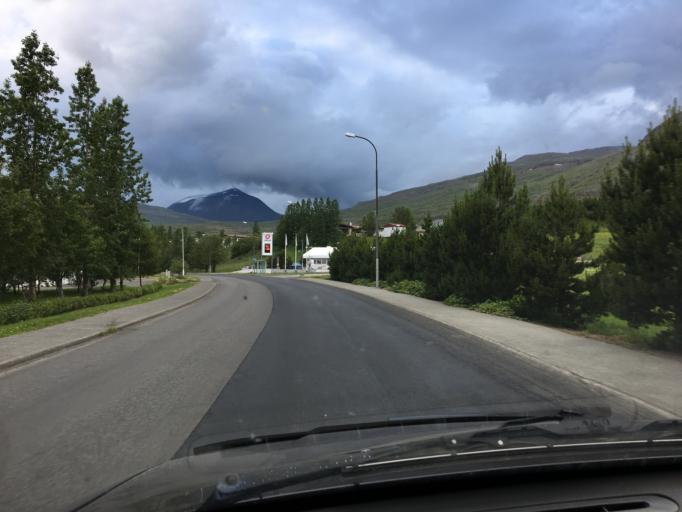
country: IS
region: East
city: Reydarfjoerdur
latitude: 65.0340
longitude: -14.2256
